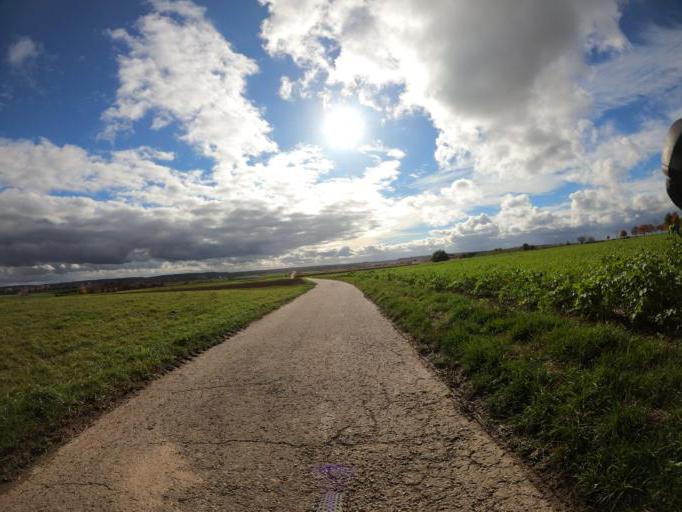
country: DE
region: Baden-Wuerttemberg
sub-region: Regierungsbezirk Stuttgart
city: Magstadt
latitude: 48.7142
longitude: 8.9563
